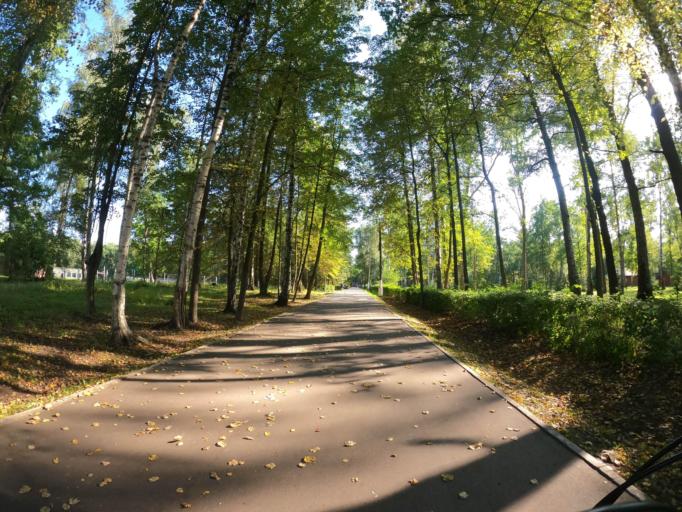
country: RU
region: Moskovskaya
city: Stupino
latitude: 54.8828
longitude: 38.0863
